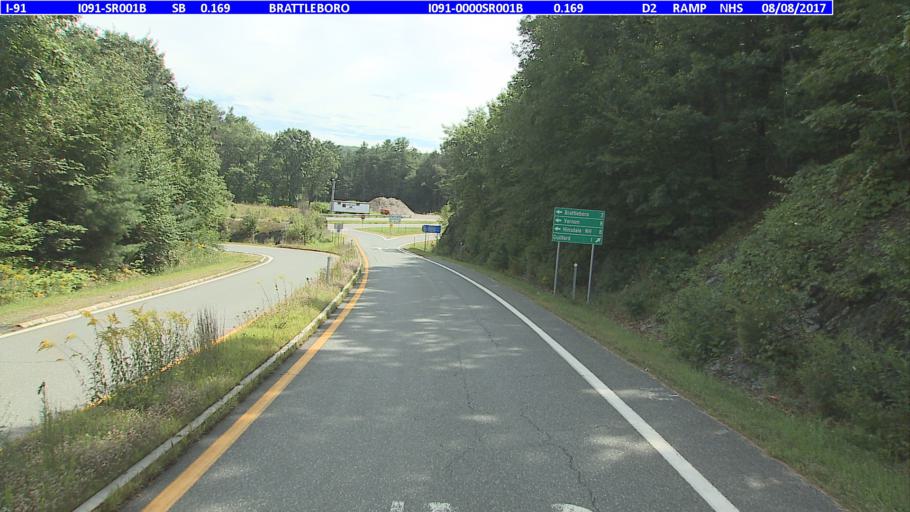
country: US
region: Vermont
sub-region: Windham County
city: Brattleboro
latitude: 42.8351
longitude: -72.5684
